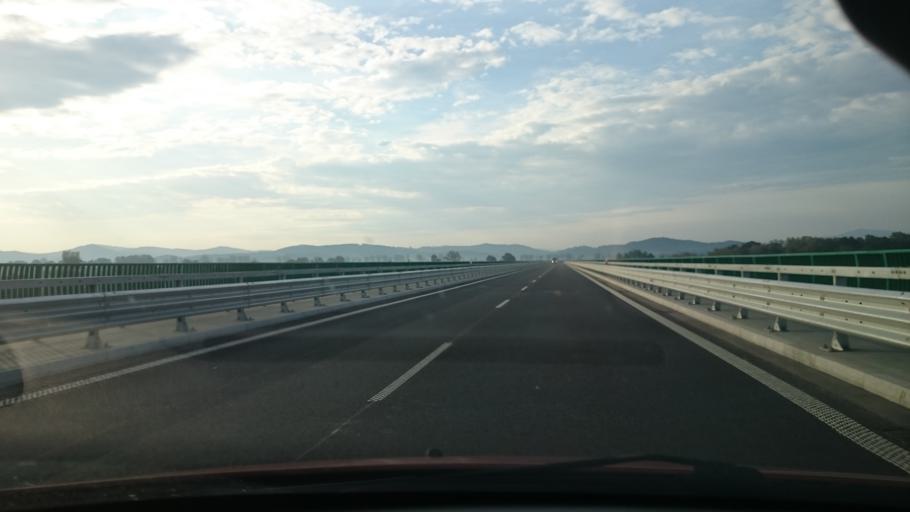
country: PL
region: Lower Silesian Voivodeship
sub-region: Powiat klodzki
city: Klodzko
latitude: 50.4057
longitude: 16.6379
